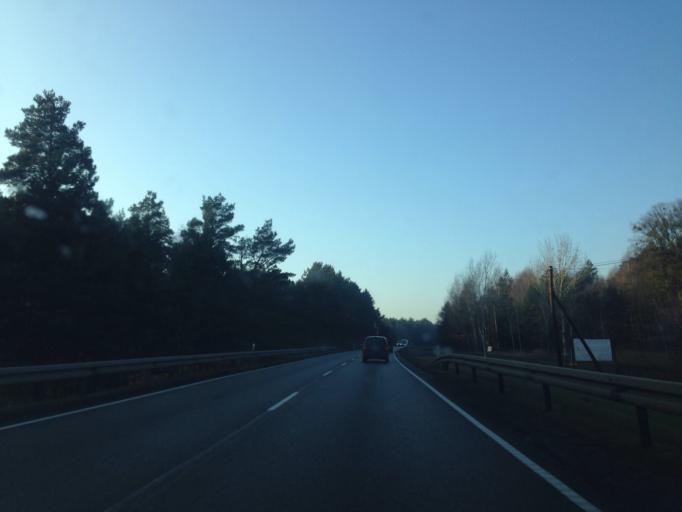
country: PL
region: Kujawsko-Pomorskie
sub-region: Powiat torunski
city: Zlawies Wielka
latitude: 53.0504
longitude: 18.3438
